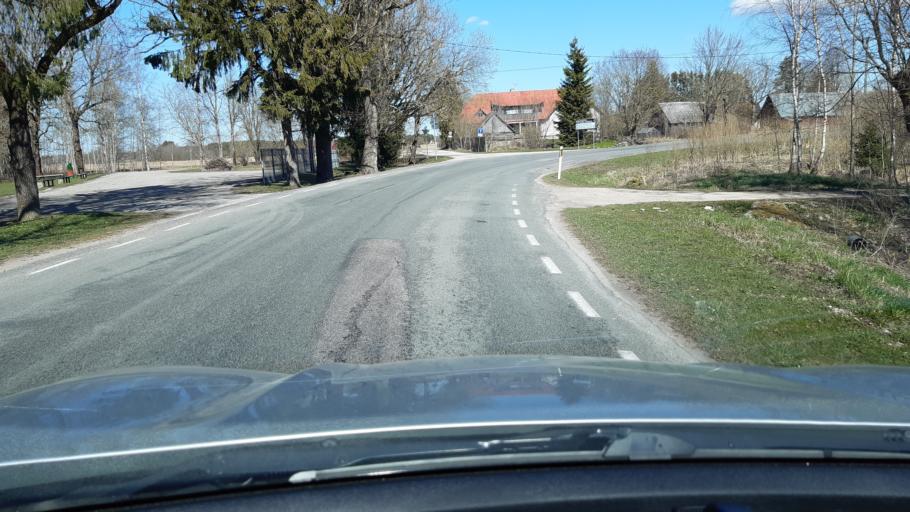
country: EE
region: Raplamaa
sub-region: Kohila vald
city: Kohila
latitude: 59.1811
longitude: 24.8530
